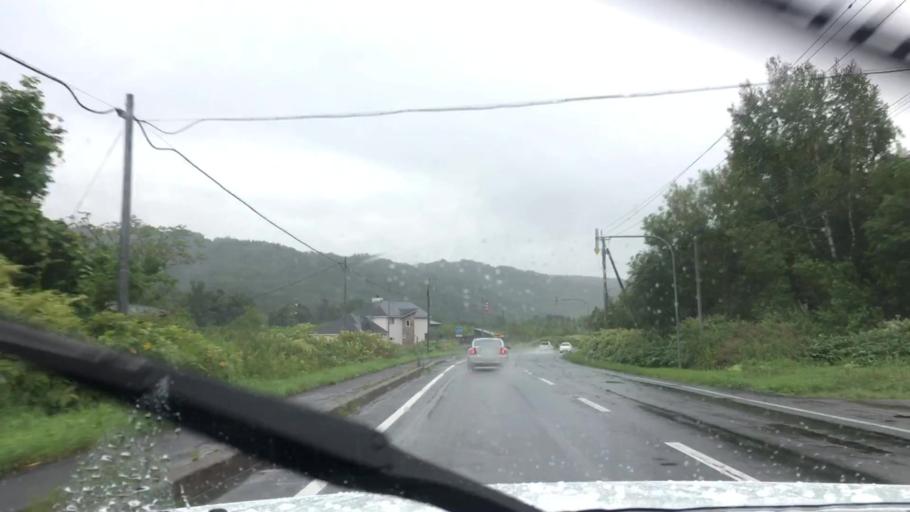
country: JP
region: Hokkaido
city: Niseko Town
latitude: 42.8097
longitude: 141.0013
